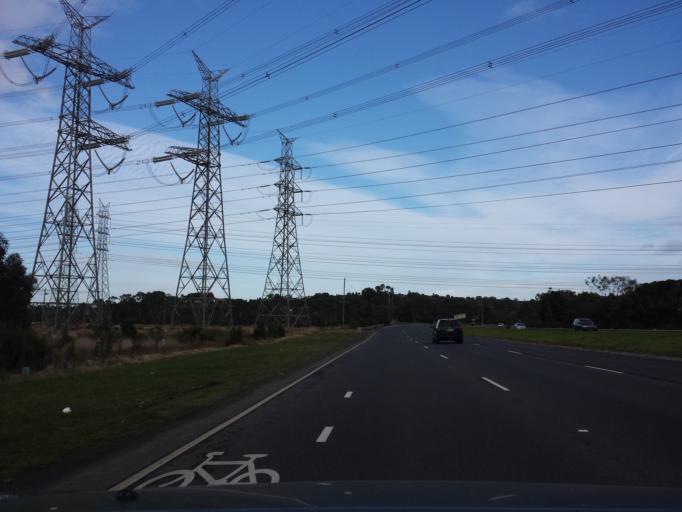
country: AU
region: Victoria
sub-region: Monash
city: Mulgrave
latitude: -37.9073
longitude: 145.2081
